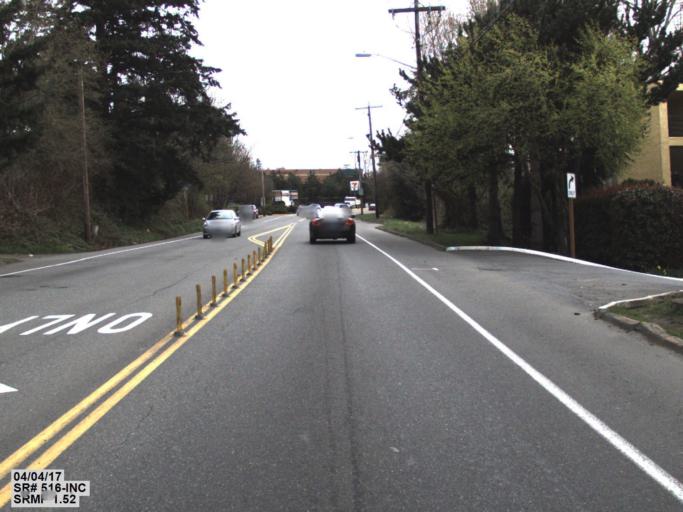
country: US
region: Washington
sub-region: King County
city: Des Moines
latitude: 47.3956
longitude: -122.2996
